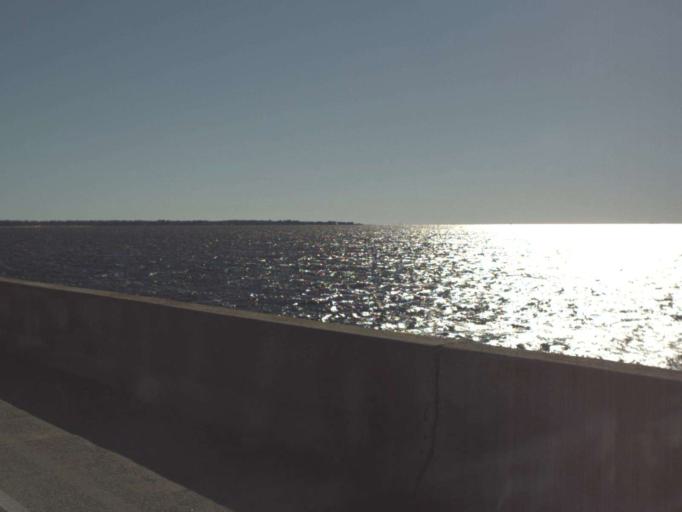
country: US
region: Florida
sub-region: Escambia County
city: East Pensacola Heights
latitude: 30.4002
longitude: -87.1872
